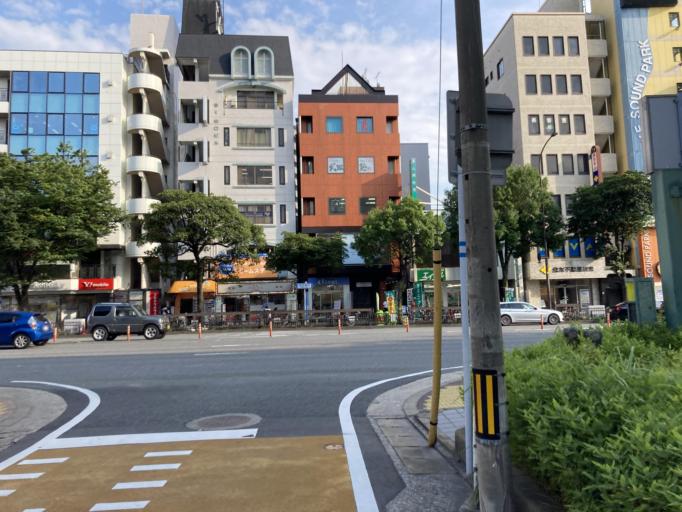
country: JP
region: Fukuoka
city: Fukuoka-shi
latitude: 33.5835
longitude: 130.3585
